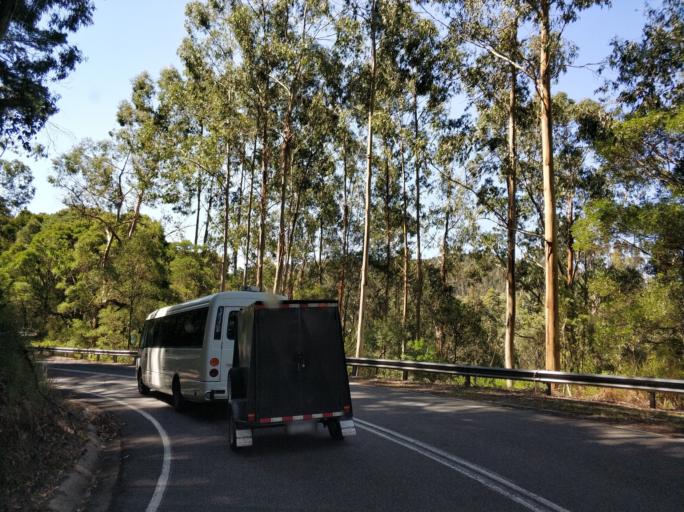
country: AU
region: Victoria
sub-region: Colac-Otway
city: Apollo Bay
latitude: -38.7317
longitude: 143.2535
